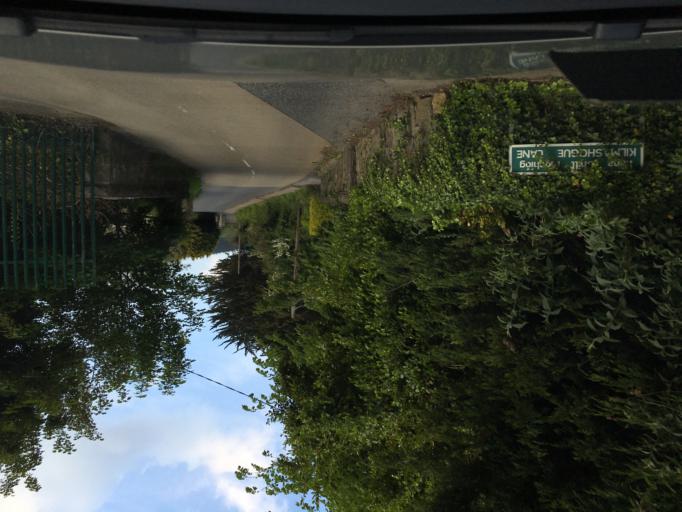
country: IE
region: Leinster
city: Ballinteer
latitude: 53.2664
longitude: -6.2800
